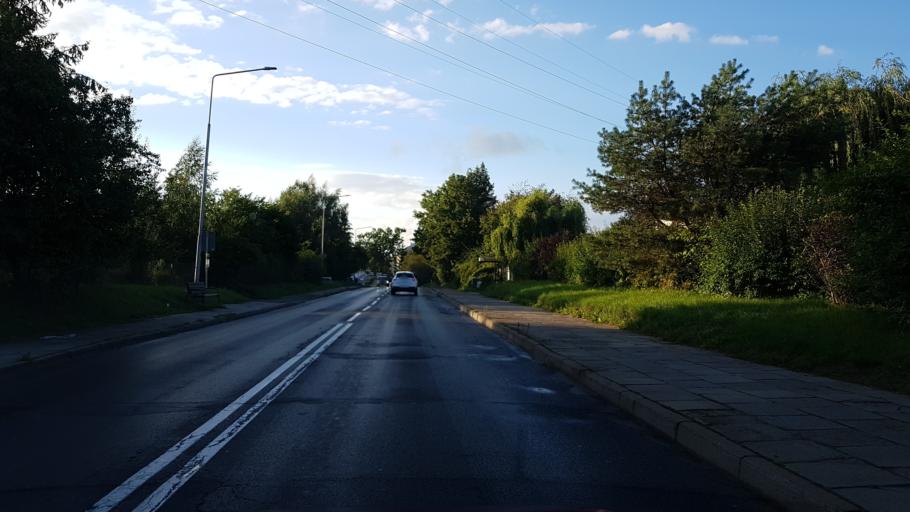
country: PL
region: West Pomeranian Voivodeship
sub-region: Koszalin
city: Koszalin
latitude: 54.2004
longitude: 16.1696
